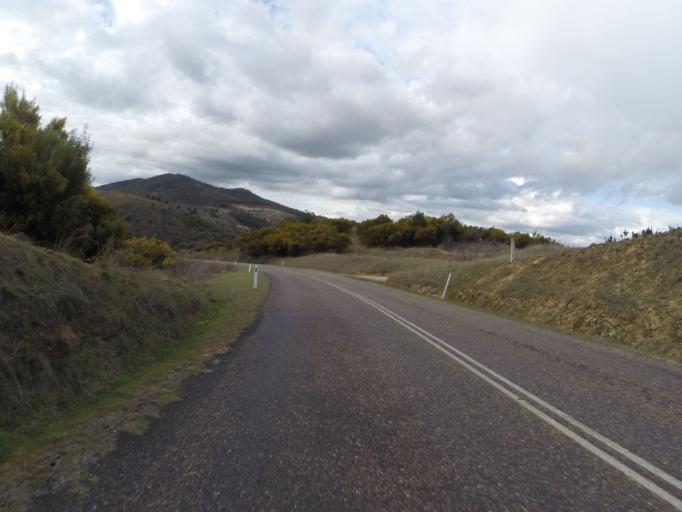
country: AU
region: Australian Capital Territory
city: Macquarie
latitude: -35.3321
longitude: 148.9339
